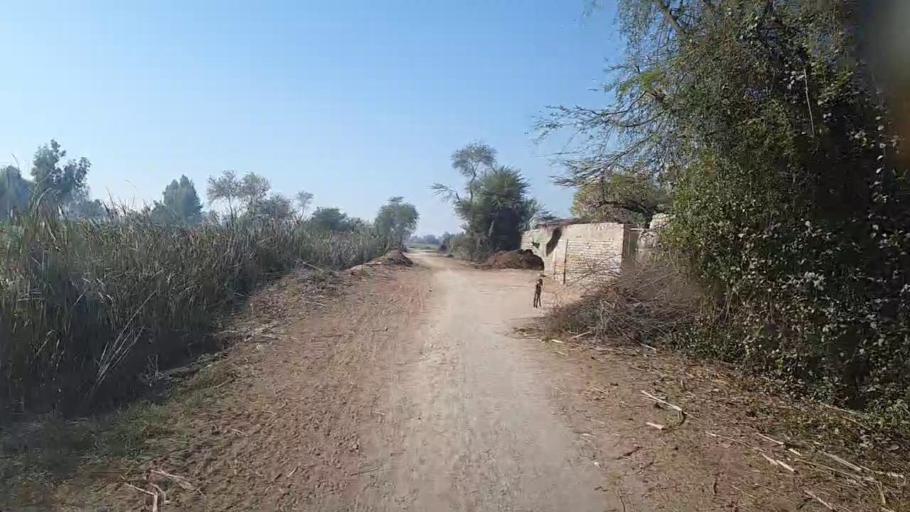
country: PK
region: Sindh
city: Khairpur
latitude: 28.0055
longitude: 69.6510
